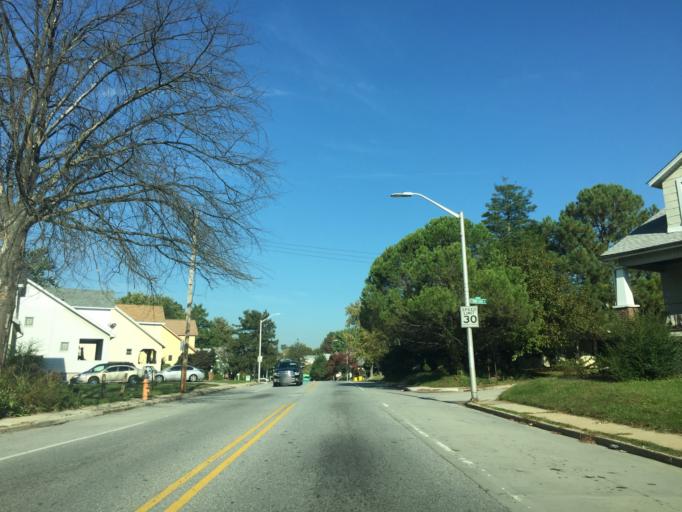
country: US
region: Maryland
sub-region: Baltimore County
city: Parkville
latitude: 39.3474
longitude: -76.5600
